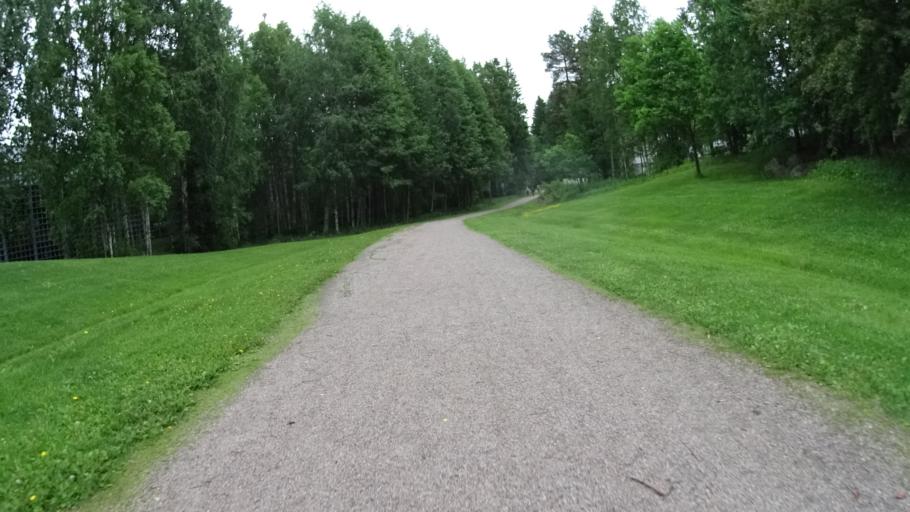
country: FI
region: Uusimaa
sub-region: Helsinki
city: Teekkarikylae
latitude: 60.2835
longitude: 24.8536
